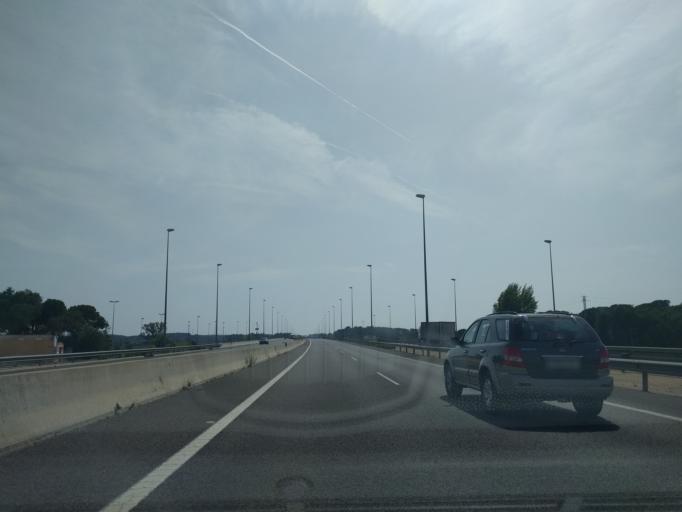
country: ES
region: Catalonia
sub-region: Provincia de Girona
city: Riudellots de la Selva
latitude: 41.8941
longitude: 2.7843
